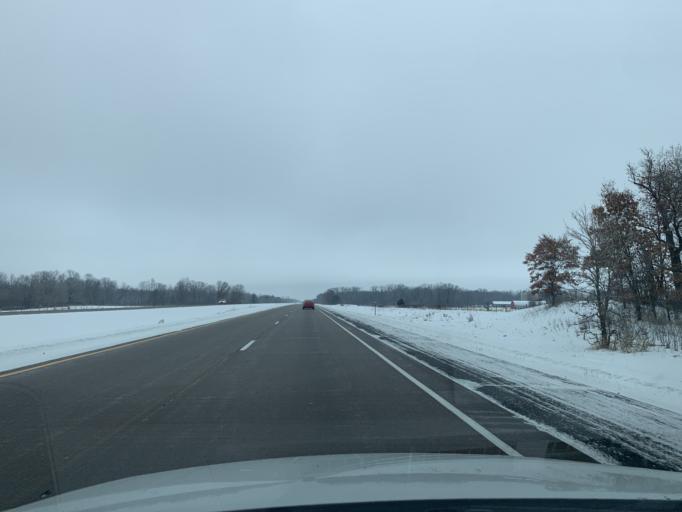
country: US
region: Minnesota
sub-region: Chisago County
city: Harris
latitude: 45.6291
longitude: -92.9921
